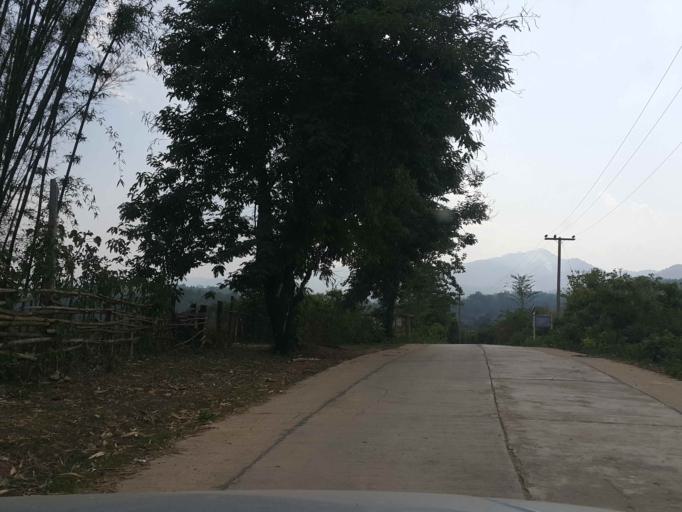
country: TH
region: Chiang Mai
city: Wiang Haeng
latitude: 19.3905
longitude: 98.7199
